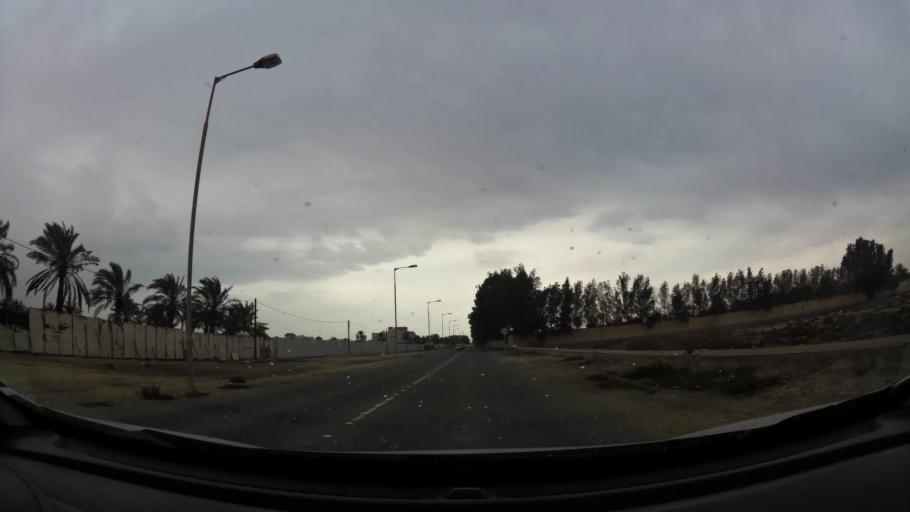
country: BH
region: Central Governorate
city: Madinat Hamad
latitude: 26.1599
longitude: 50.4599
